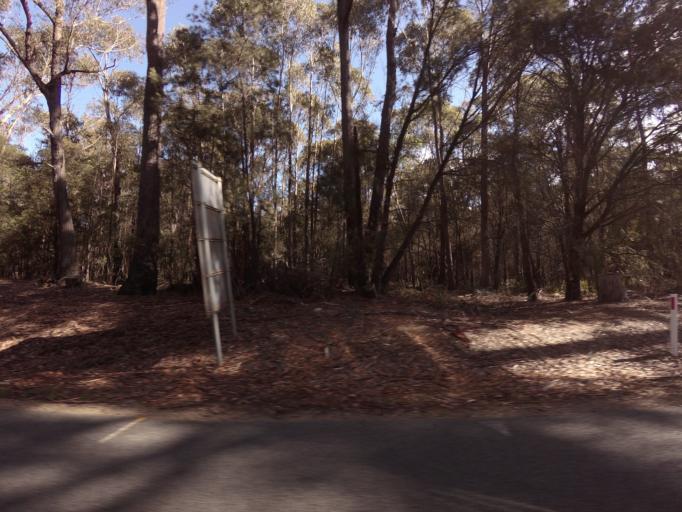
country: AU
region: Tasmania
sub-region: Break O'Day
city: St Helens
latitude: -41.6619
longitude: 148.2779
